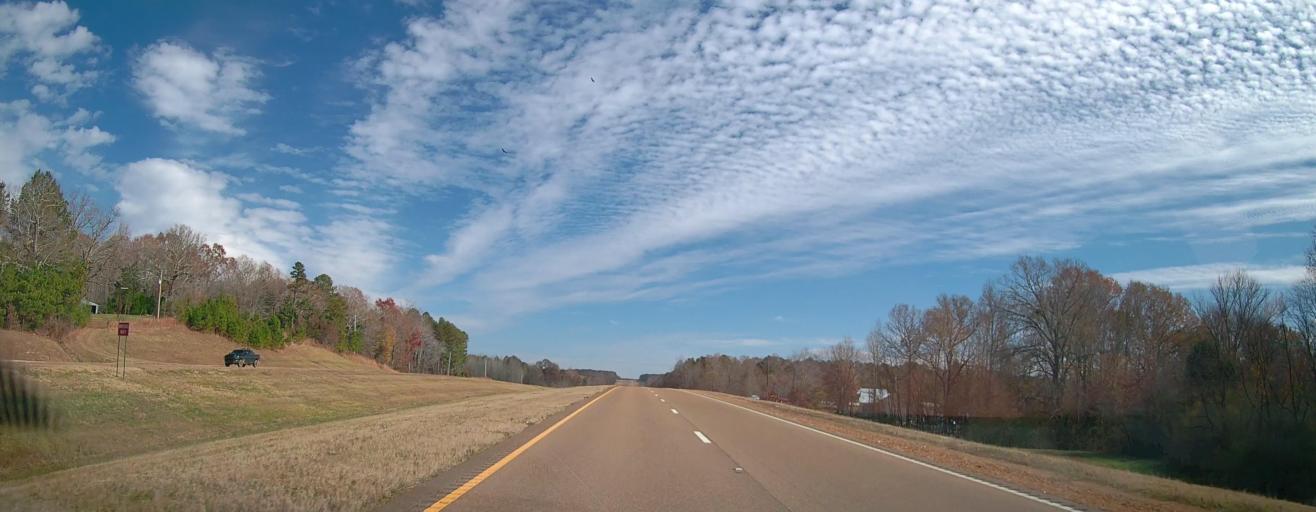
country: US
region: Mississippi
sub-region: Benton County
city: Ashland
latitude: 34.9511
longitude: -89.0715
